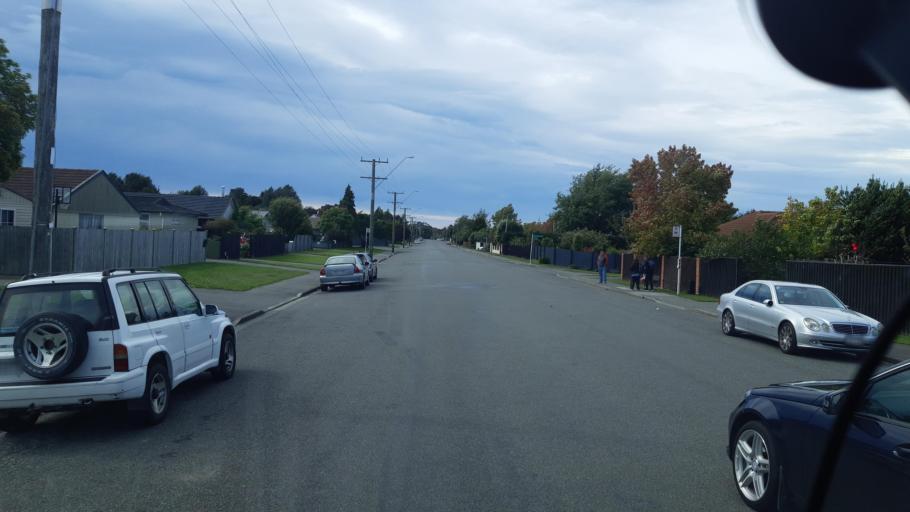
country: NZ
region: Canterbury
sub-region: Waimakariri District
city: Woodend
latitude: -43.3205
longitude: 172.6597
